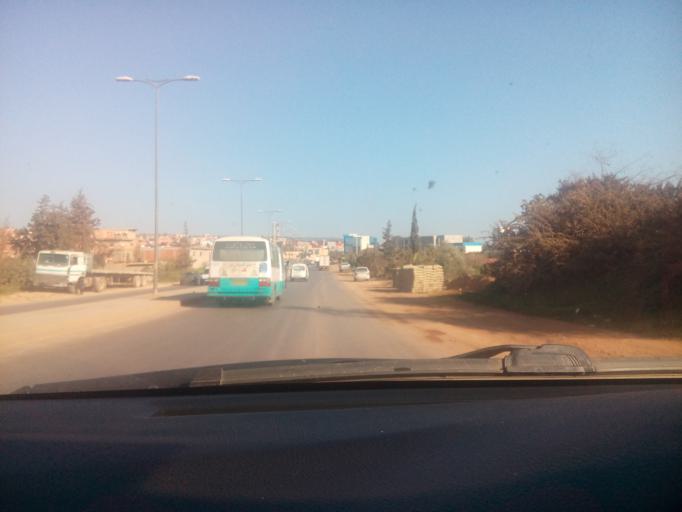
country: DZ
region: Oran
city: Oran
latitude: 35.6555
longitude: -0.6978
